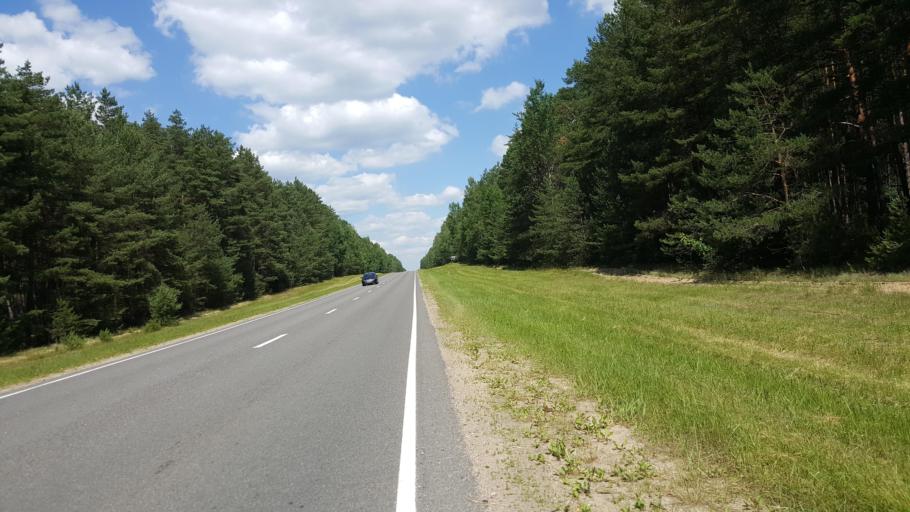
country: BY
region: Brest
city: Kamyanyuki
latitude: 52.5059
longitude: 23.7880
